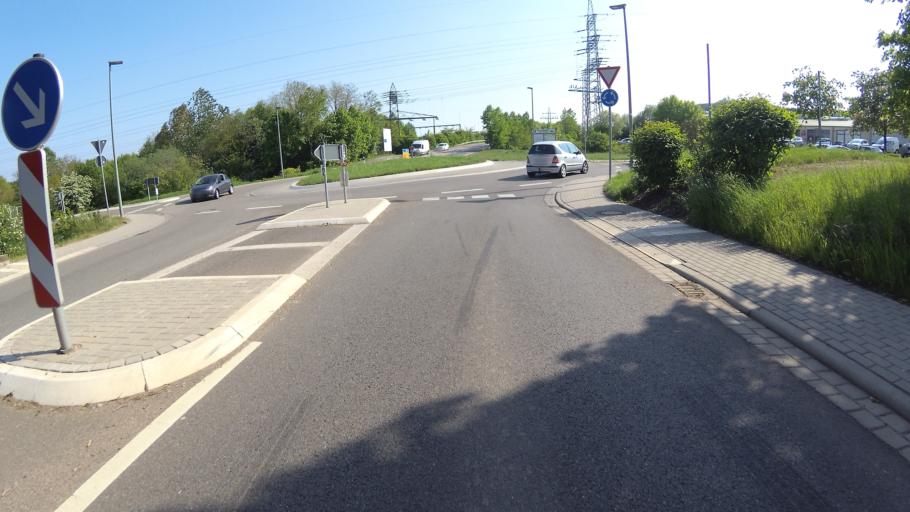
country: DE
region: Saarland
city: Merchweiler
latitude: 49.3463
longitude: 7.0496
